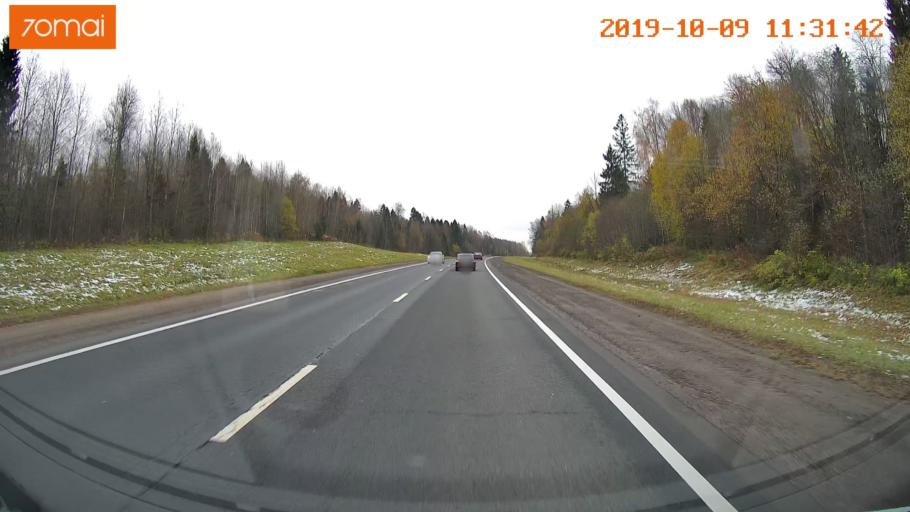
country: RU
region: Vologda
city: Gryazovets
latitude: 59.0430
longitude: 40.1010
